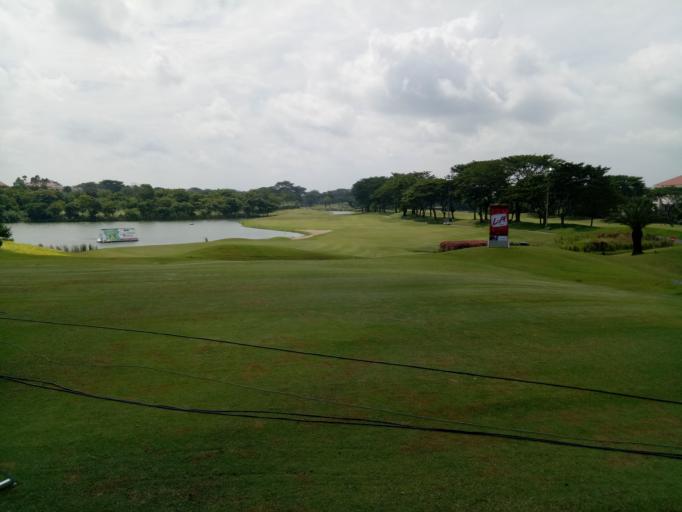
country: ID
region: East Java
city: Driyorejo
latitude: -7.2932
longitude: 112.6370
